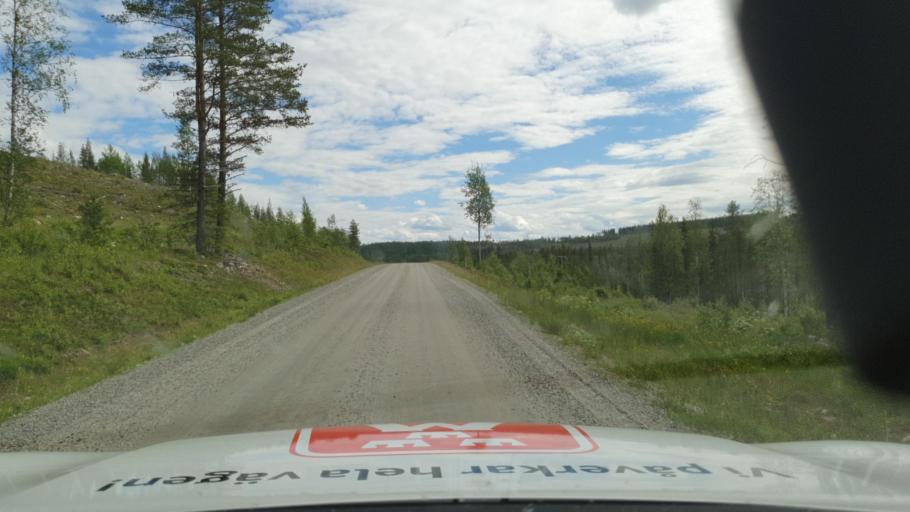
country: SE
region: Vaesterbotten
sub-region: Norsjo Kommun
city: Norsjoe
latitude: 64.8424
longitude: 19.5260
